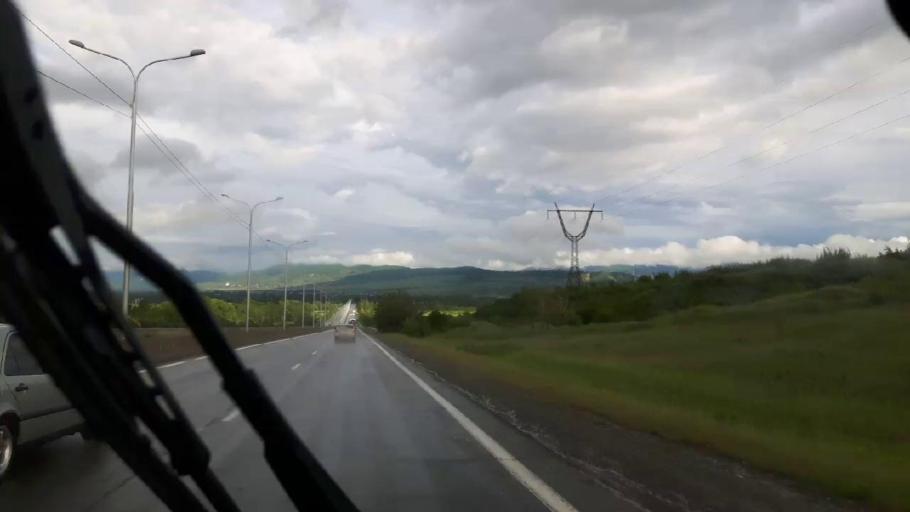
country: GE
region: Shida Kartli
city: Kaspi
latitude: 41.9275
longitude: 44.5333
